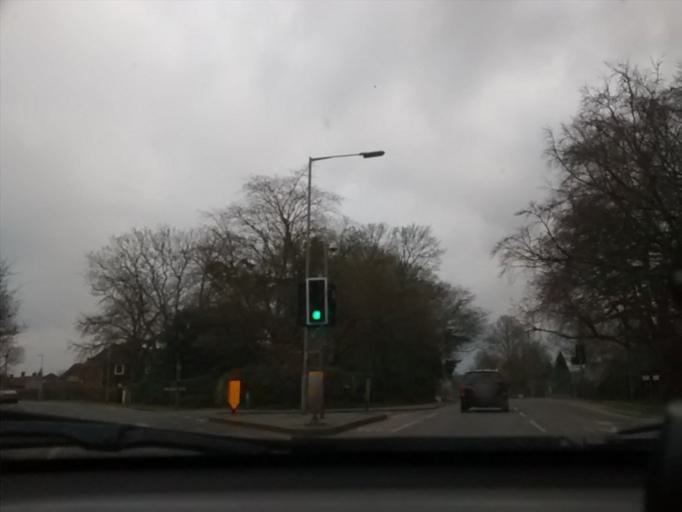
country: GB
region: England
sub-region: Cambridgeshire
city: Cambridge
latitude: 52.1744
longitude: 0.1483
